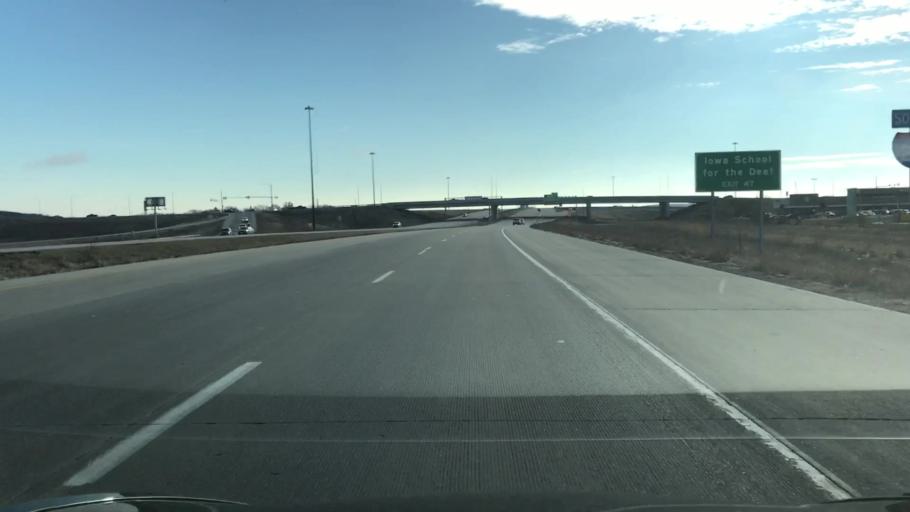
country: US
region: Iowa
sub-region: Pottawattamie County
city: Council Bluffs
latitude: 41.2236
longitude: -95.8353
